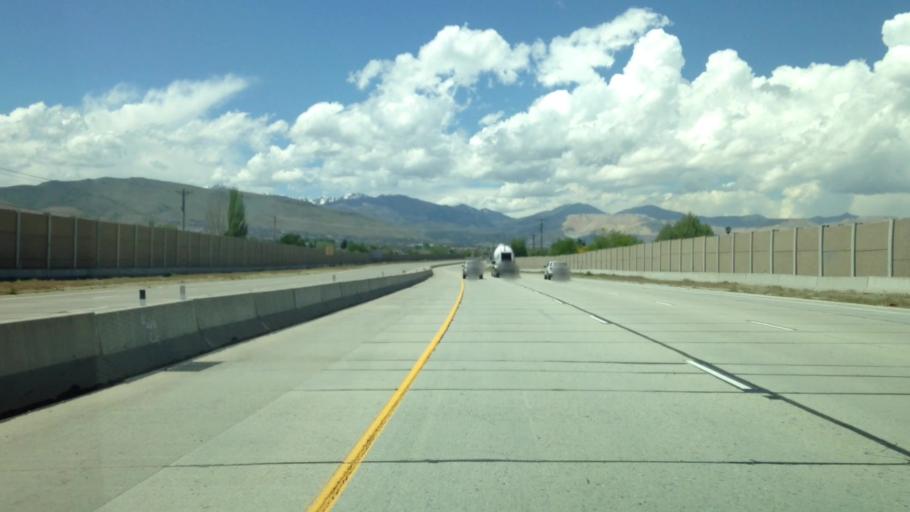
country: US
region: Utah
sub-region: Salt Lake County
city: Bluffdale
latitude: 40.5010
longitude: -111.9459
